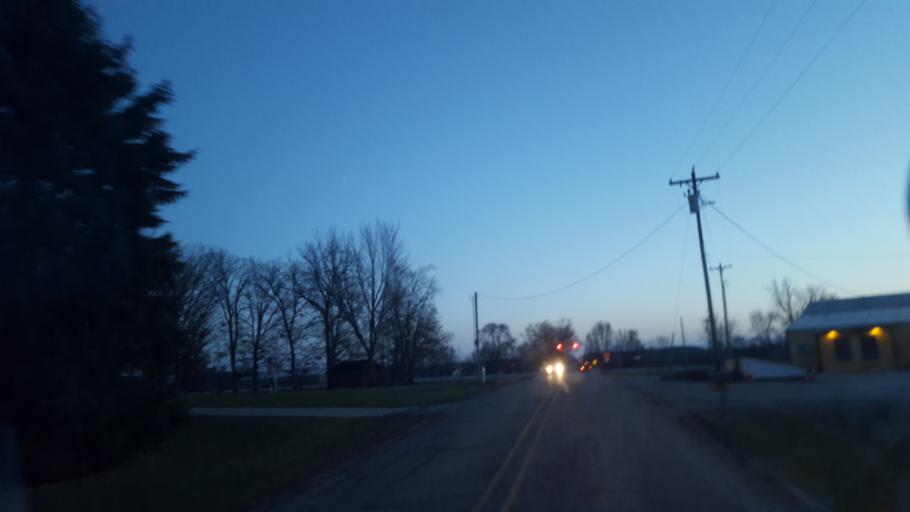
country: US
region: Indiana
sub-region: Kosciusko County
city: Mentone
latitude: 41.2685
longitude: -85.9986
